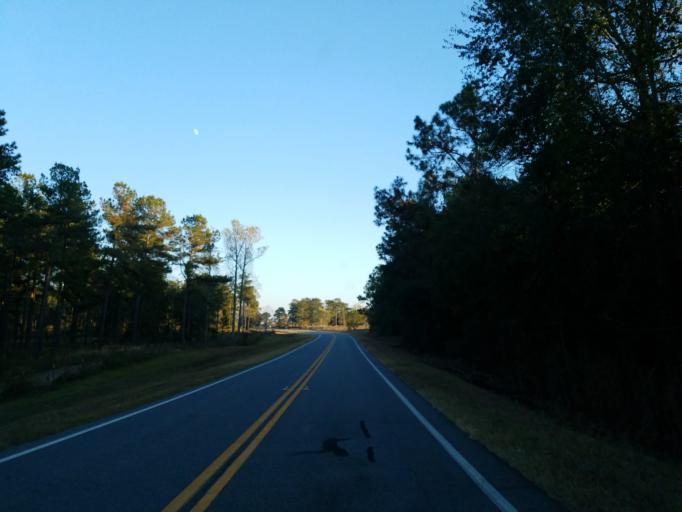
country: US
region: Georgia
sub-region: Wilcox County
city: Rochelle
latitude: 31.8183
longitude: -83.5370
